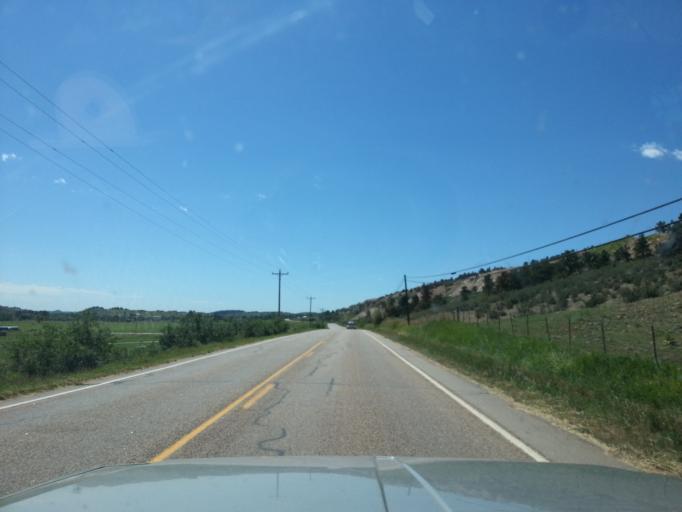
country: US
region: Colorado
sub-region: Larimer County
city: Loveland
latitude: 40.4502
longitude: -105.2043
